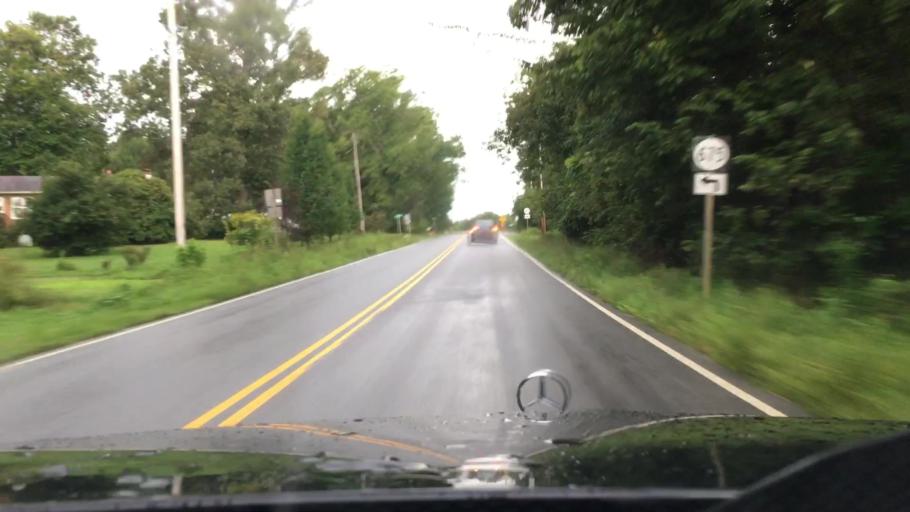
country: US
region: Virginia
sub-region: Amherst County
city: Amherst
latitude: 37.7165
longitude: -79.0205
